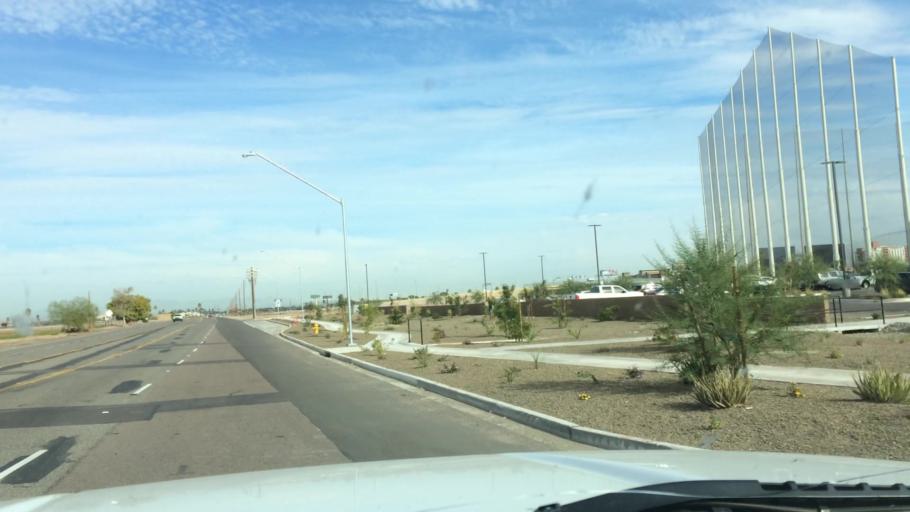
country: US
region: Arizona
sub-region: Maricopa County
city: Peoria
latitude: 33.5240
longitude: -112.2723
